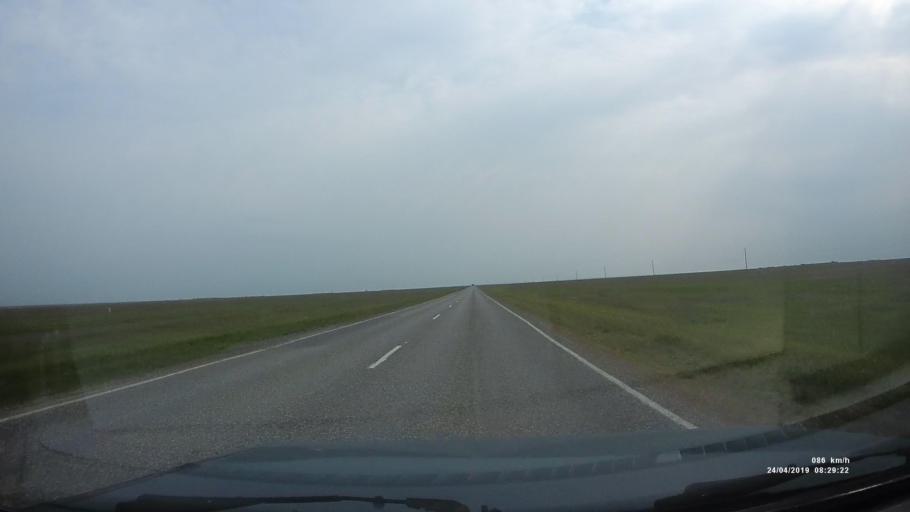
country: RU
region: Kalmykiya
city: Priyutnoye
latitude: 46.1518
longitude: 43.8300
